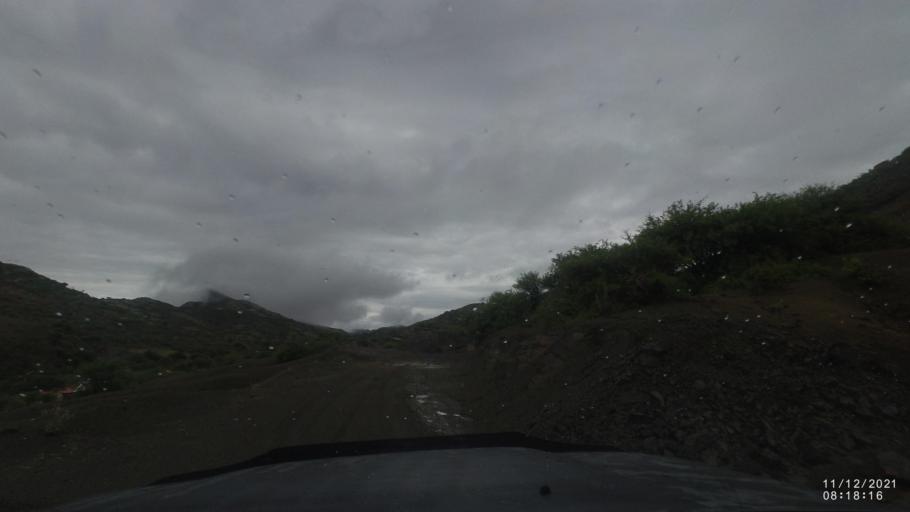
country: BO
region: Cochabamba
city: Tarata
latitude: -17.9419
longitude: -65.9292
